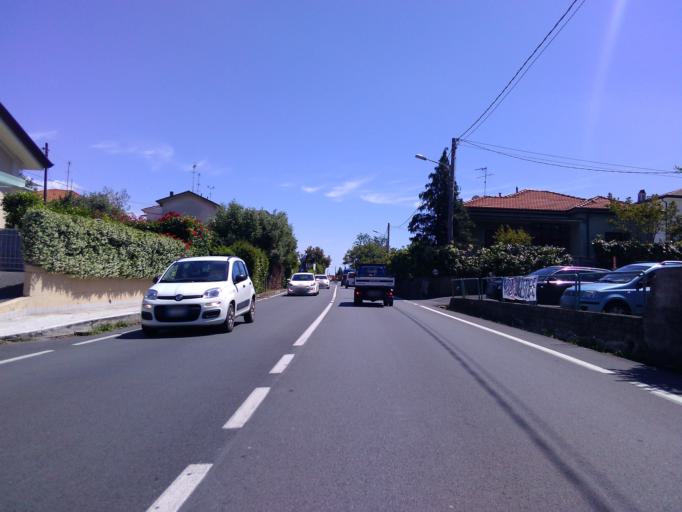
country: IT
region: Liguria
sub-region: Provincia di La Spezia
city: Santo Stefano di Magra
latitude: 44.1508
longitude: 9.9205
